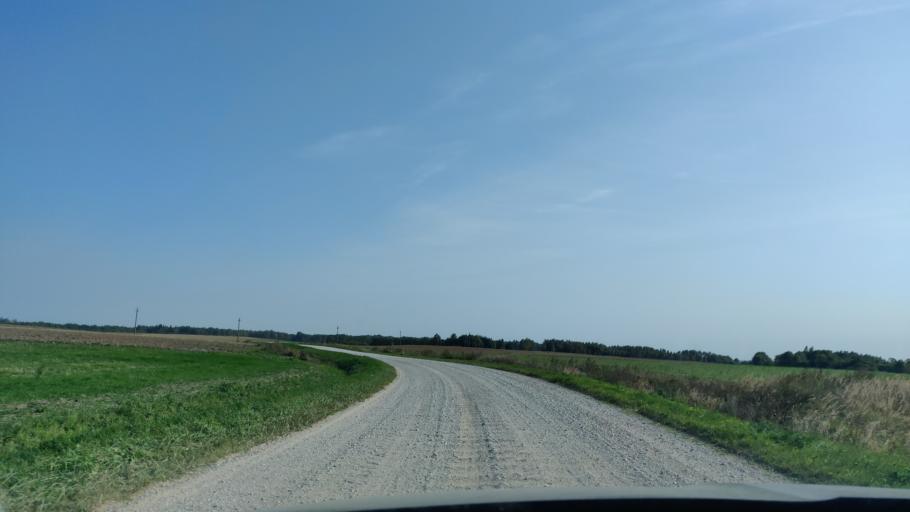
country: LT
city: Sirvintos
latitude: 54.9686
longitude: 24.8428
